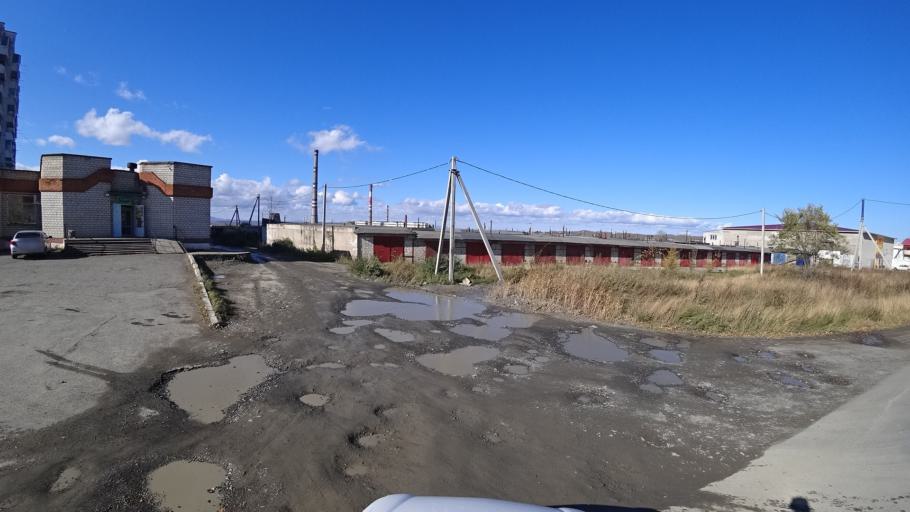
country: RU
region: Khabarovsk Krai
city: Amursk
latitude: 50.2191
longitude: 136.8958
